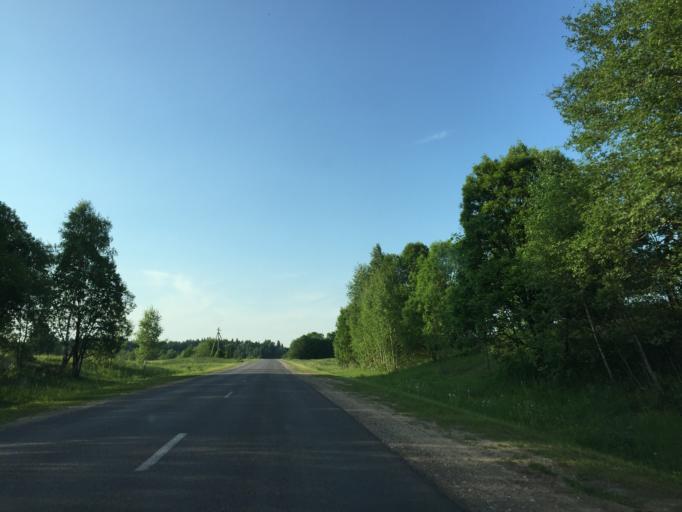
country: LT
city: Plateliai
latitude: 56.0557
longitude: 21.8195
